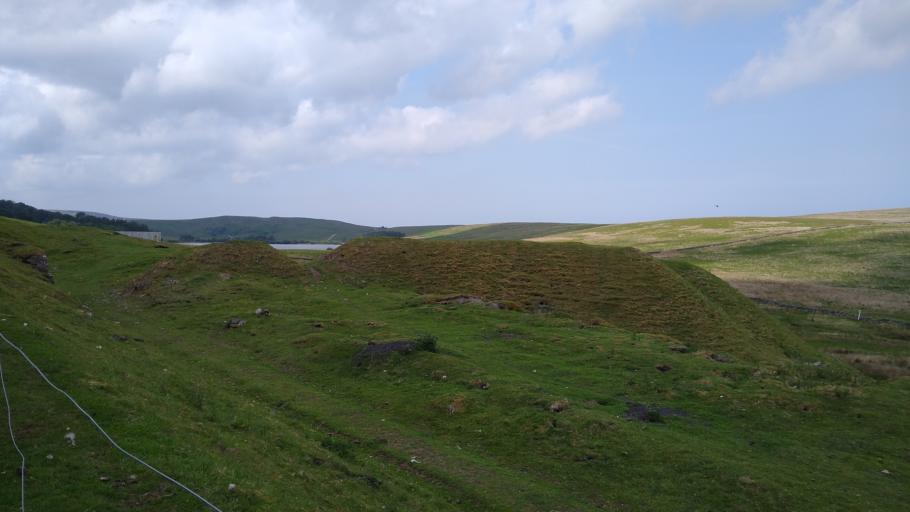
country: GB
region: England
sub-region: Northumberland
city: Greenhead
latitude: 54.9241
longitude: -2.6034
